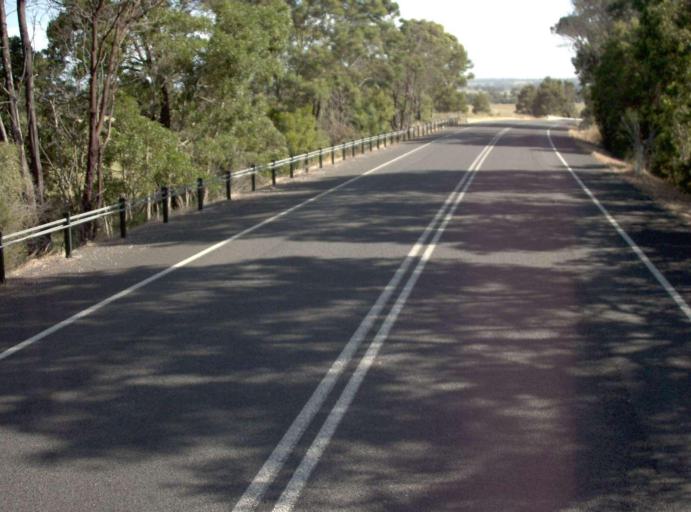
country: AU
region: Victoria
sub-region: East Gippsland
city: Lakes Entrance
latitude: -37.8530
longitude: 147.8456
